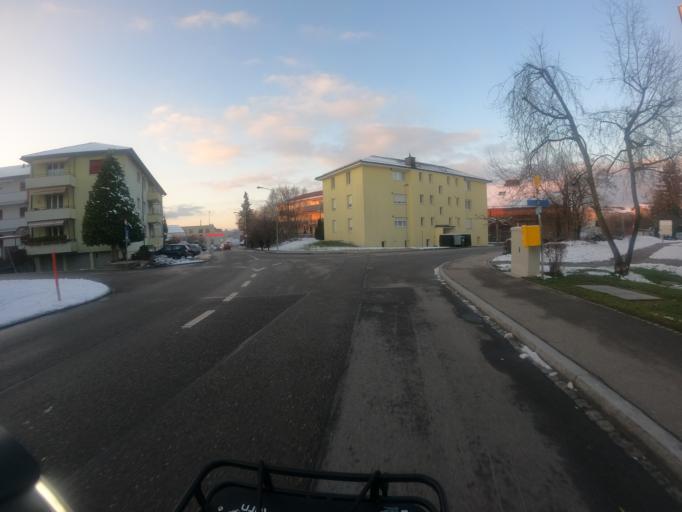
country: CH
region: Zurich
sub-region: Bezirk Affoltern
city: Affoltern / Hasenbueel
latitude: 47.2719
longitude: 8.4494
